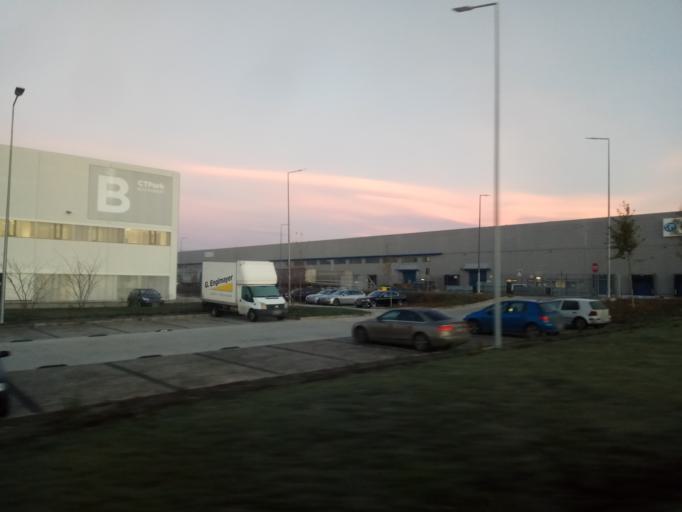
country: RO
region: Ilfov
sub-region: Comuna Dragomiresti-Vale
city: Dragomiresti-Deal
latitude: 44.4399
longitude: 25.9374
